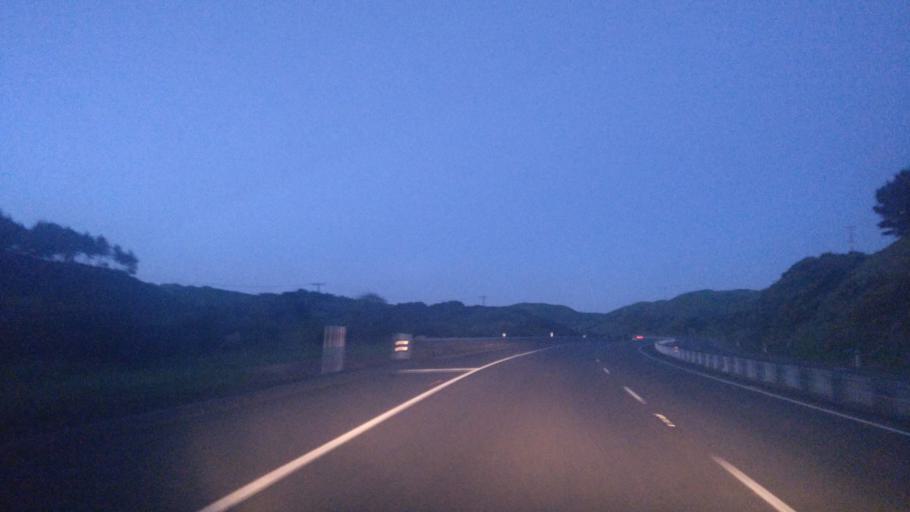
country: NZ
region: Wellington
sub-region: Porirua City
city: Porirua
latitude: -41.0720
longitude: 174.8755
